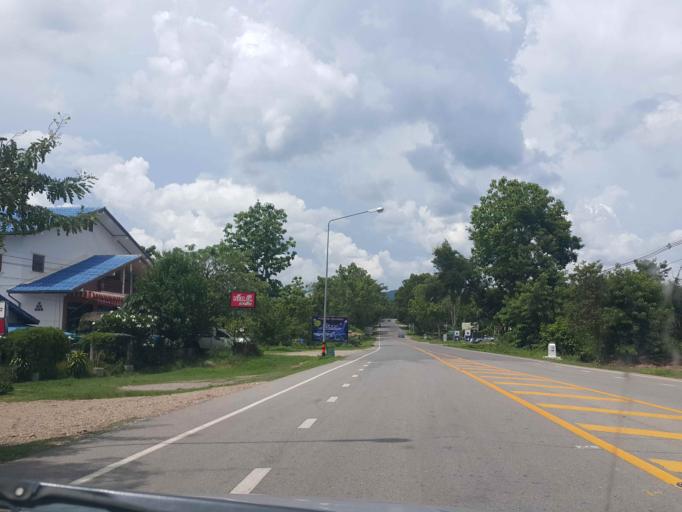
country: TH
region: Nan
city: Ban Luang
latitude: 18.8507
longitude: 100.4449
